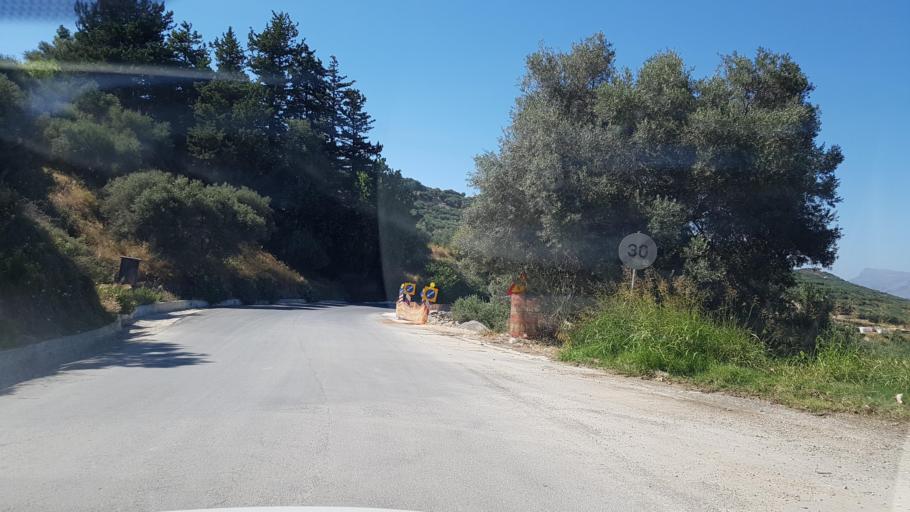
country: GR
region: Crete
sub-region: Nomos Chanias
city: Kissamos
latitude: 35.4304
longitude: 23.6874
